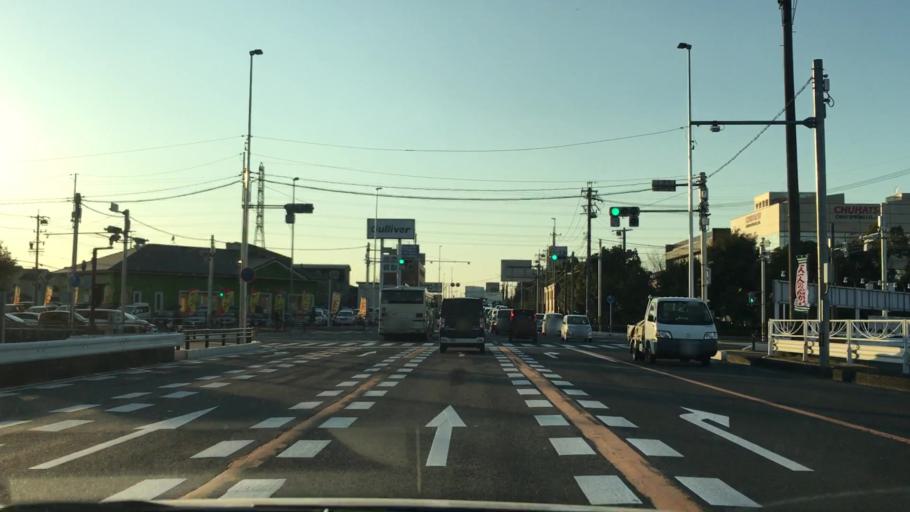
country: JP
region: Aichi
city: Obu
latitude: 35.0782
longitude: 136.9451
